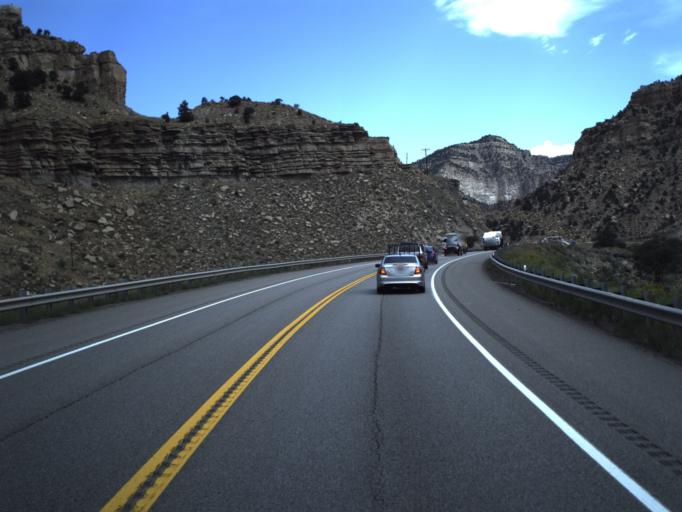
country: US
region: Utah
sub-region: Carbon County
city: Helper
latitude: 39.7079
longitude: -110.8696
